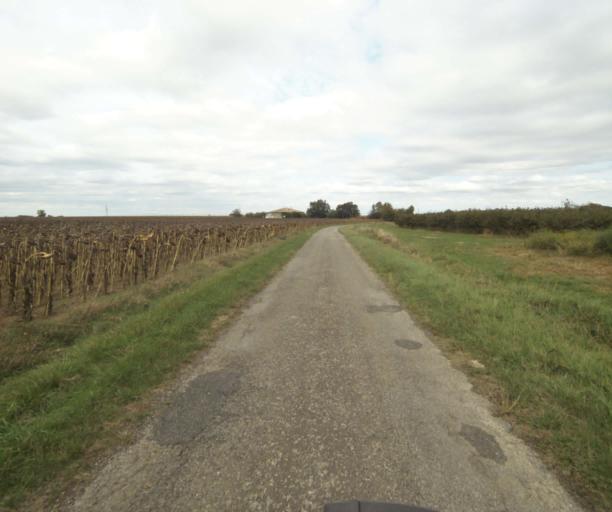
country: FR
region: Midi-Pyrenees
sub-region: Departement du Tarn-et-Garonne
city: Verdun-sur-Garonne
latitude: 43.8667
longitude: 1.1556
